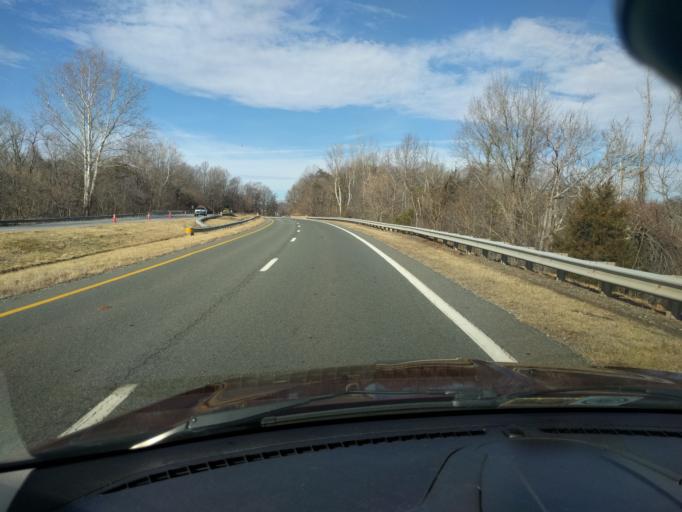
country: US
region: Virginia
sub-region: Amherst County
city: Madison Heights
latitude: 37.5139
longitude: -79.1162
